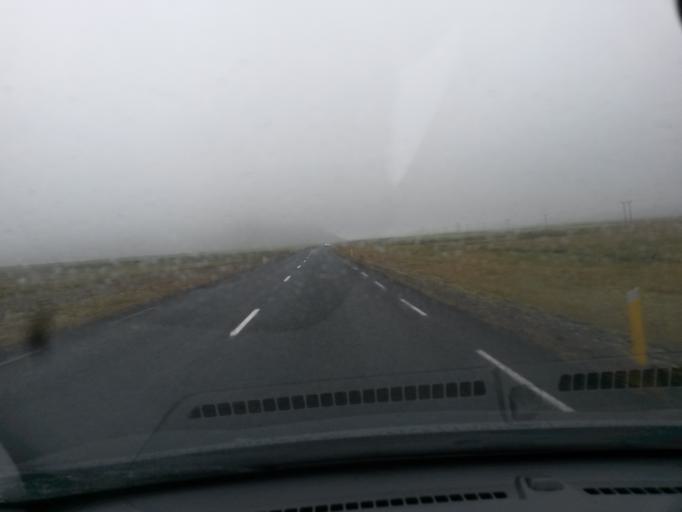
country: IS
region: South
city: Vestmannaeyjar
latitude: 63.4622
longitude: -19.2308
